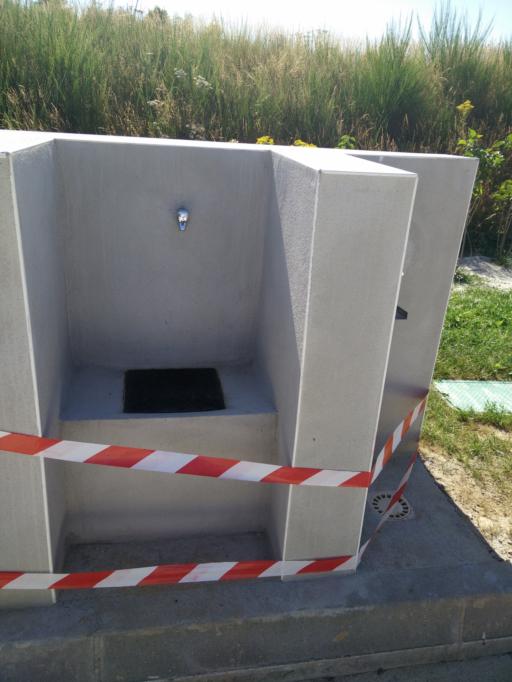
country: FR
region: Brittany
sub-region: Departement du Morbihan
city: Colpo
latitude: 47.8159
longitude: -2.8117
